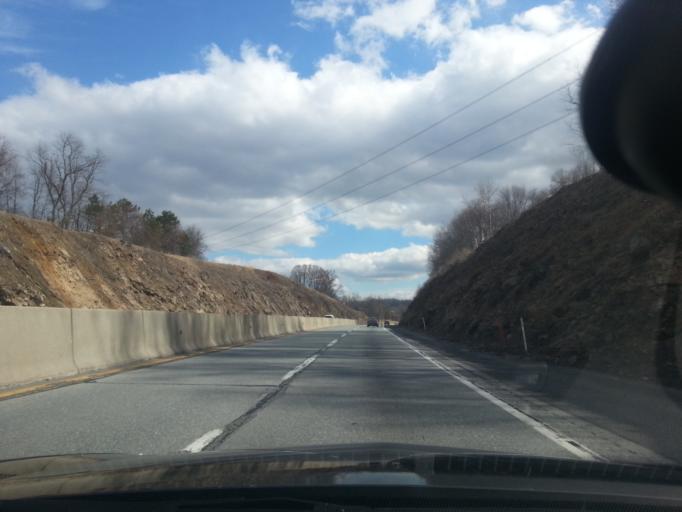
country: US
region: Pennsylvania
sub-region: Lehigh County
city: Emmaus
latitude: 40.4901
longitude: -75.4694
